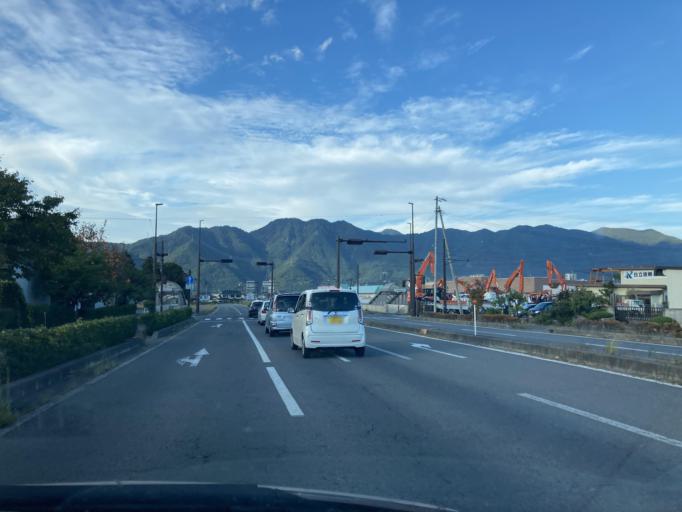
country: JP
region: Nagano
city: Ueda
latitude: 36.3904
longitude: 138.2093
